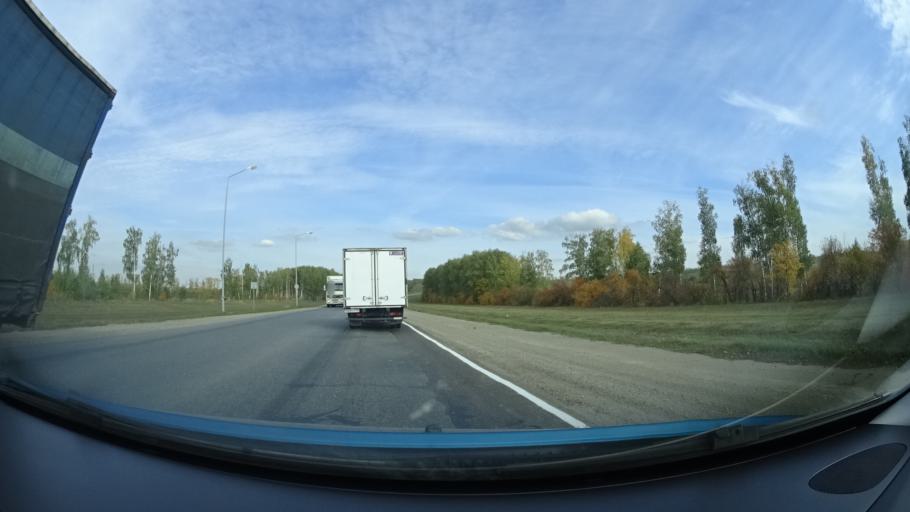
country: RU
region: Bashkortostan
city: Kandry
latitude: 54.5417
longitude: 54.1383
